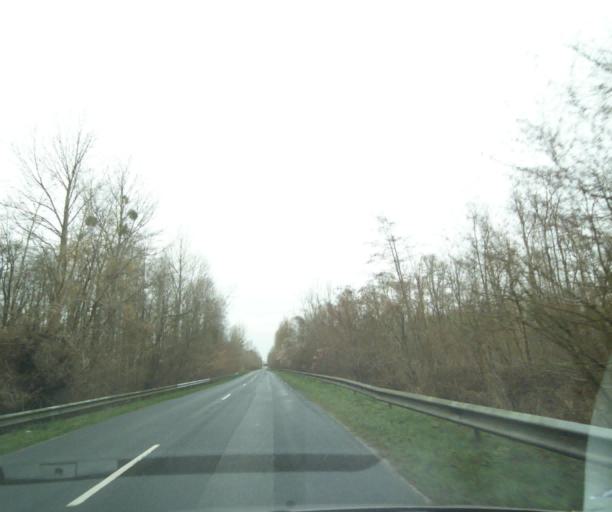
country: FR
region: Picardie
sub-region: Departement de l'Oise
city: Noyon
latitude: 49.5606
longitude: 3.0356
